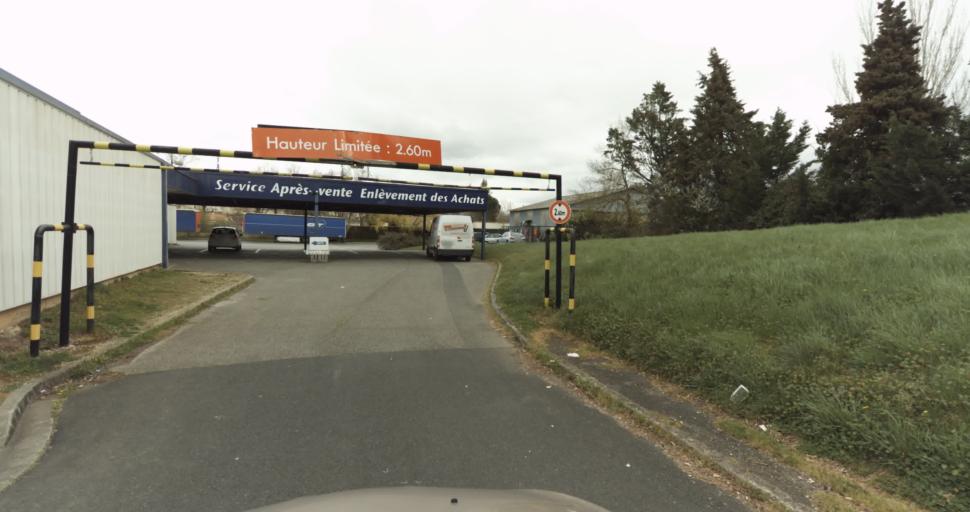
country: FR
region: Midi-Pyrenees
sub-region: Departement du Tarn
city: Puygouzon
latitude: 43.8885
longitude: 2.1664
